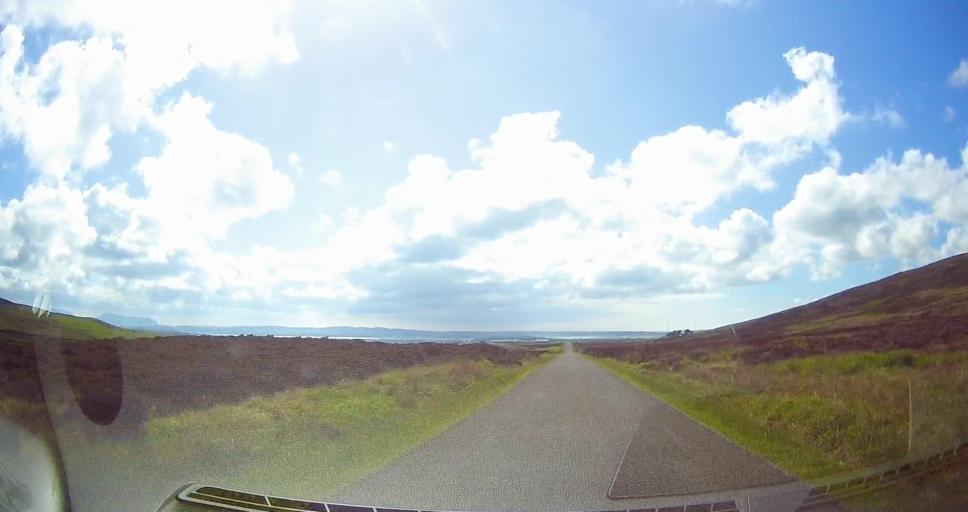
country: GB
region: Scotland
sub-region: Orkney Islands
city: Stromness
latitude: 59.0470
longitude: -3.1333
